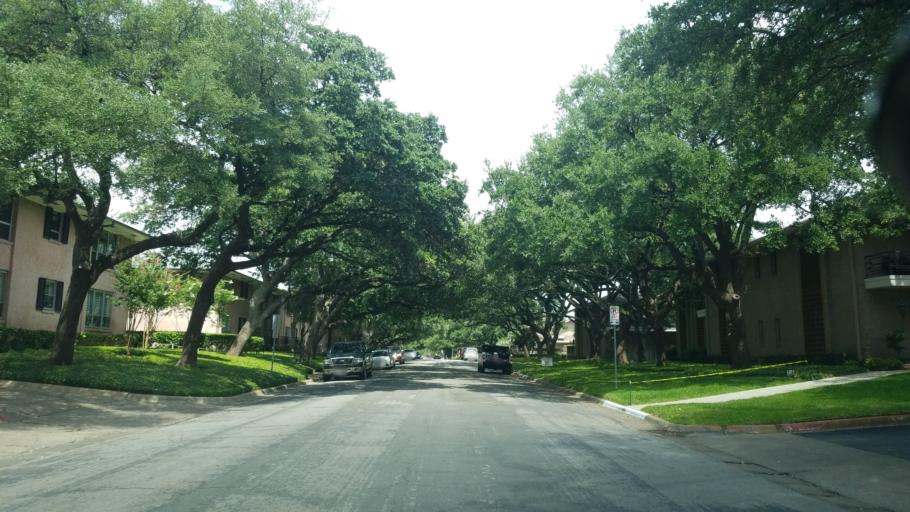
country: US
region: Texas
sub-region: Dallas County
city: University Park
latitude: 32.8675
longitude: -96.7988
